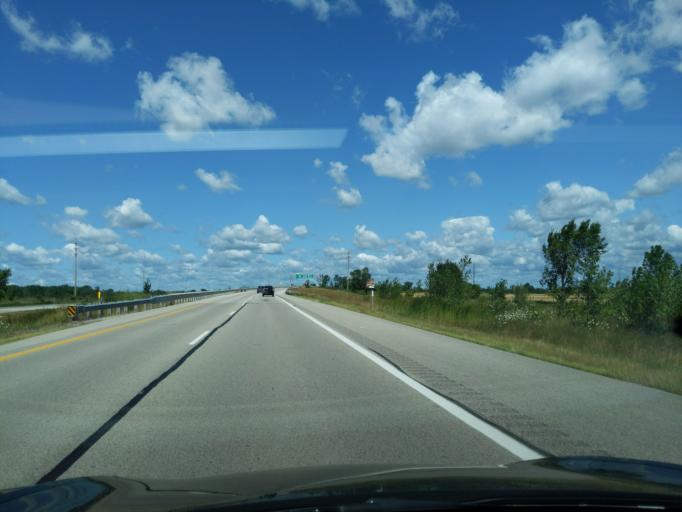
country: US
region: Michigan
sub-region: Isabella County
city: Shepherd
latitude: 43.5611
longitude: -84.7299
